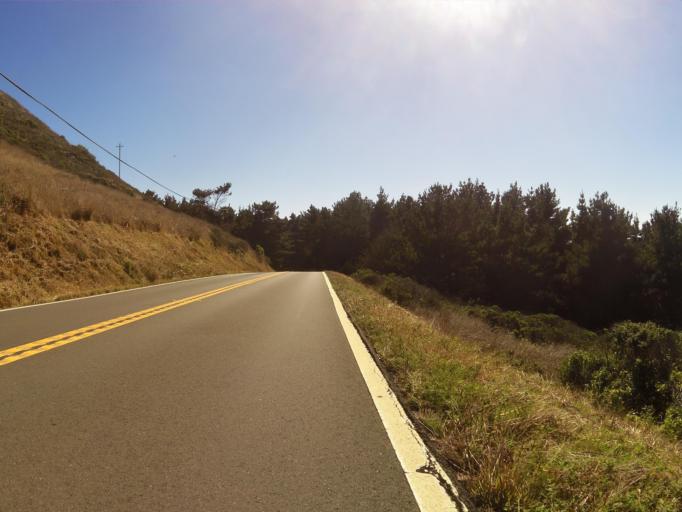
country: US
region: California
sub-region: Mendocino County
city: Fort Bragg
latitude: 39.6029
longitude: -123.7854
